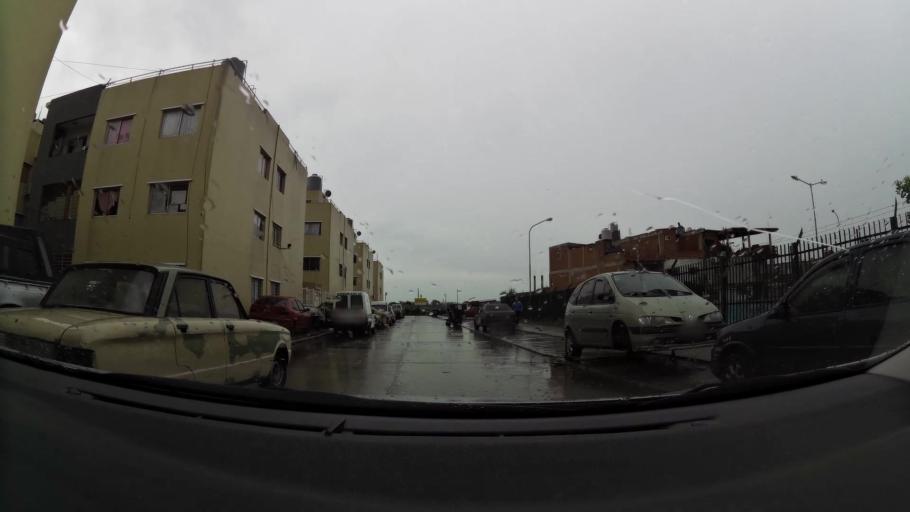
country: AR
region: Buenos Aires F.D.
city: Villa Lugano
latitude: -34.6643
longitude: -58.4561
